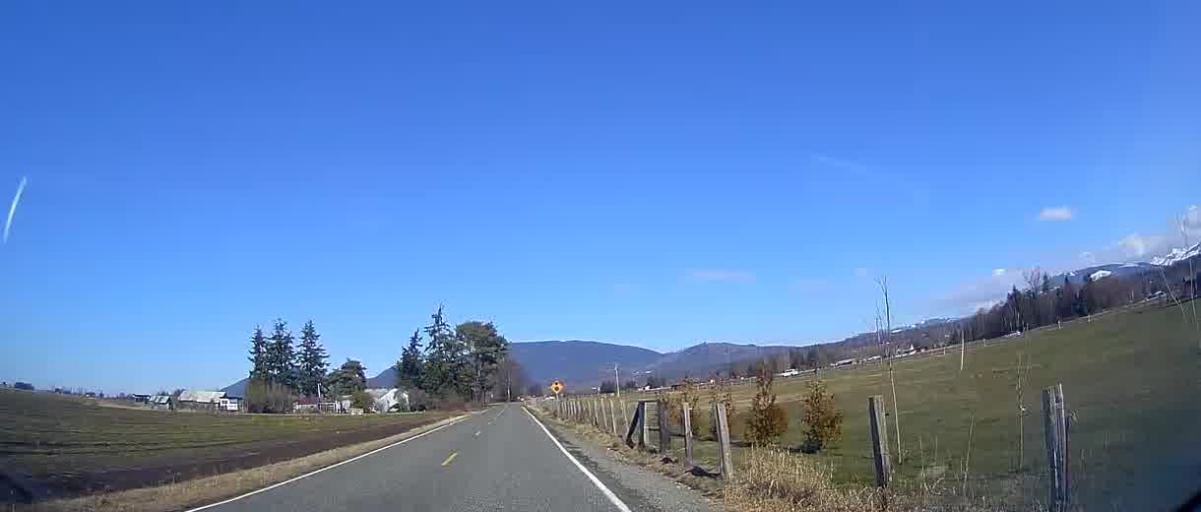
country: US
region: Washington
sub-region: Skagit County
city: Burlington
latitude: 48.5491
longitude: -122.4113
